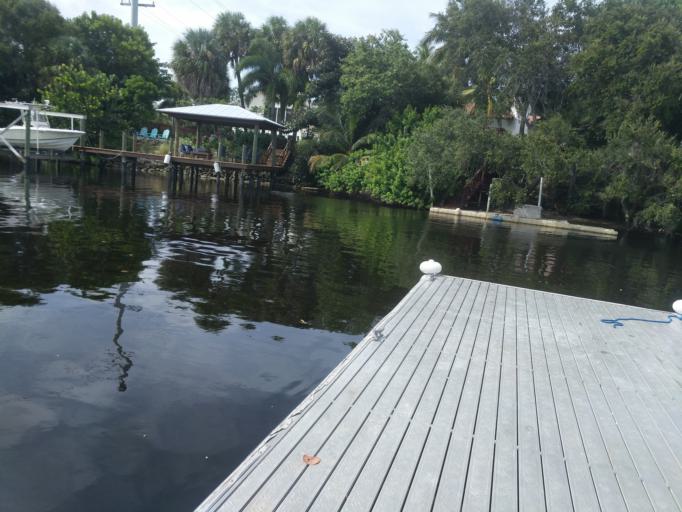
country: US
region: Florida
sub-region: Broward County
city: Deerfield Beach
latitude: 26.3278
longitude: -80.1035
